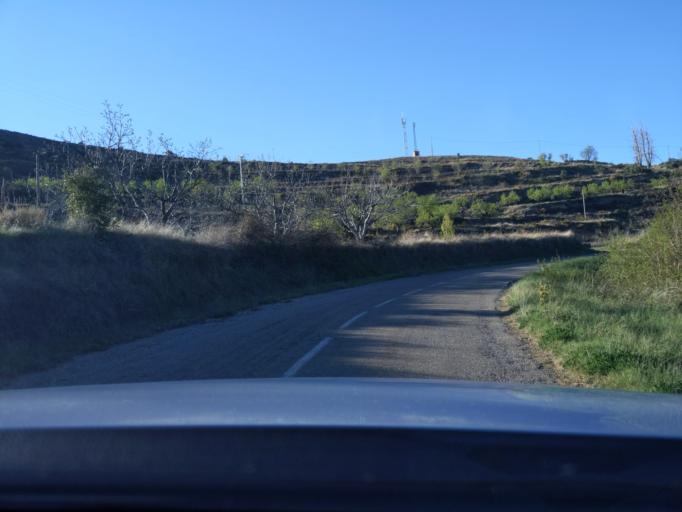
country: ES
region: La Rioja
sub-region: Provincia de La Rioja
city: Bergasillas Bajera
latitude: 42.2431
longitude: -2.1616
